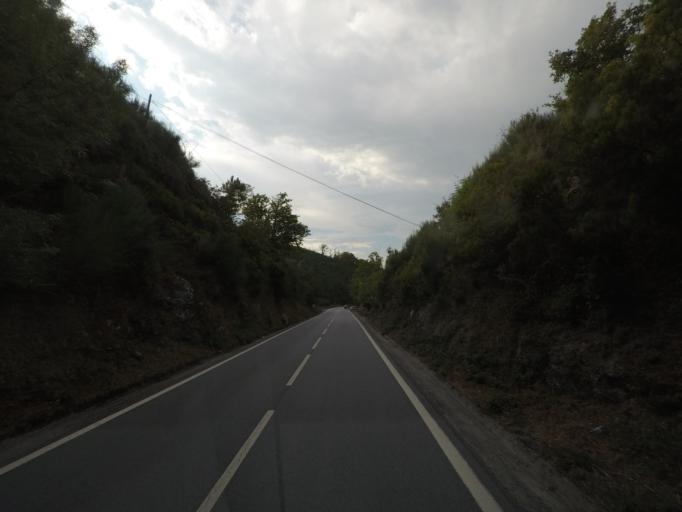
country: PT
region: Porto
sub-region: Baiao
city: Valadares
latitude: 41.2053
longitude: -7.9717
